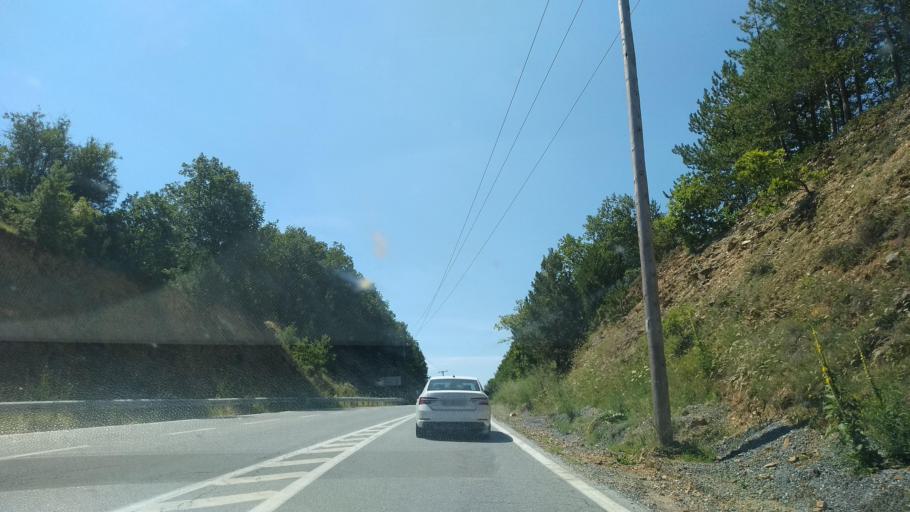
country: GR
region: Central Macedonia
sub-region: Nomos Chalkidikis
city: Megali Panagia
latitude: 40.4573
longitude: 23.6572
